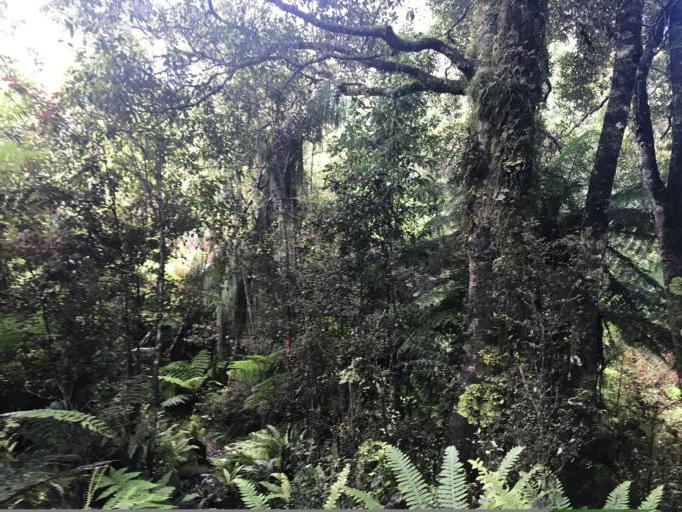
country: NZ
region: West Coast
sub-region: Westland District
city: Hokitika
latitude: -42.7629
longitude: 171.2454
